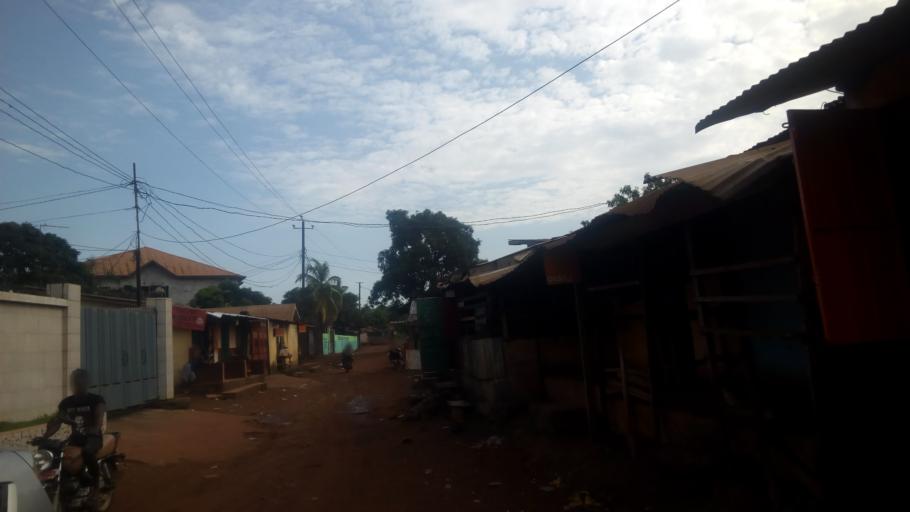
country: GN
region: Kindia
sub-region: Prefecture de Dubreka
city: Dubreka
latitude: 9.6525
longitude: -13.5345
